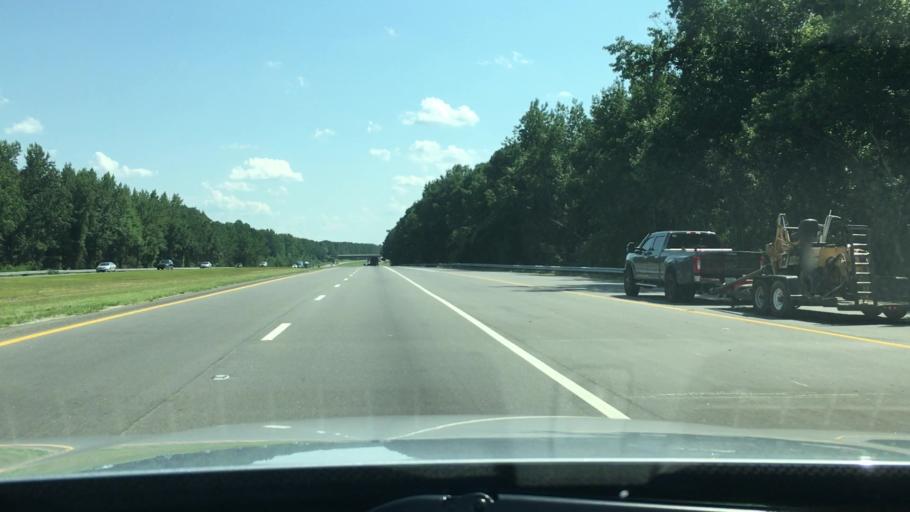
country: US
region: North Carolina
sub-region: Cumberland County
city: Vander
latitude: 35.0343
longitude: -78.8062
